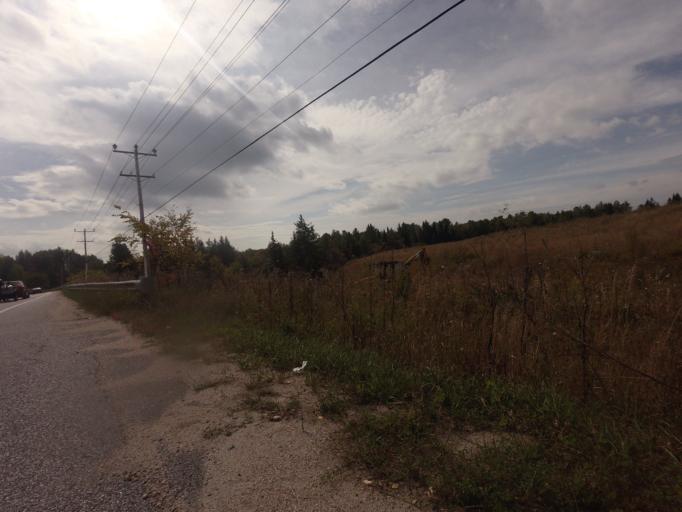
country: CA
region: Quebec
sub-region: Outaouais
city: Wakefield
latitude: 45.8520
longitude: -75.9967
